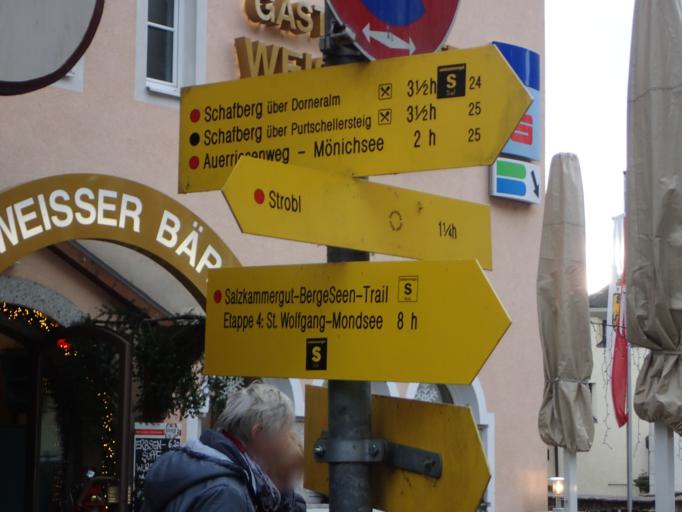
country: AT
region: Upper Austria
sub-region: Politischer Bezirk Gmunden
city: Sankt Wolfgang im Salzkammergut
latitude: 47.7385
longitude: 13.4479
